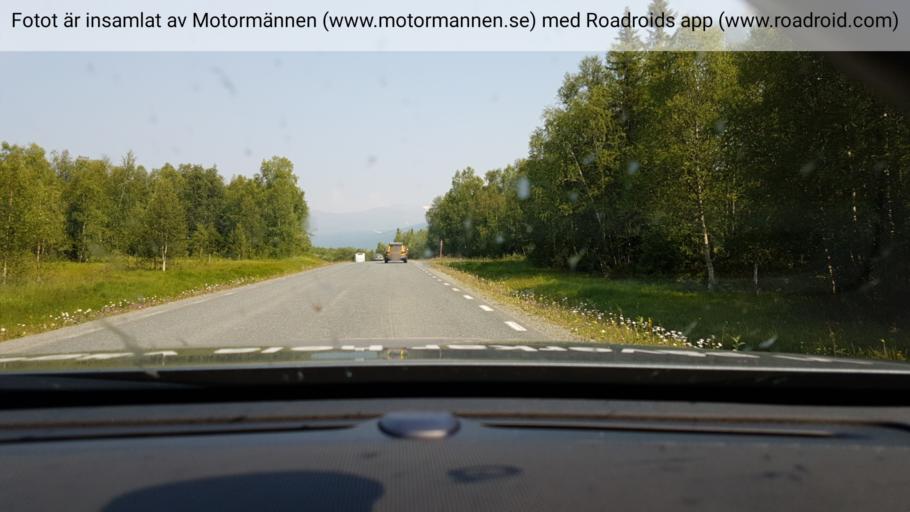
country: NO
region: Nordland
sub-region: Rana
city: Mo i Rana
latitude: 65.7588
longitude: 15.1156
